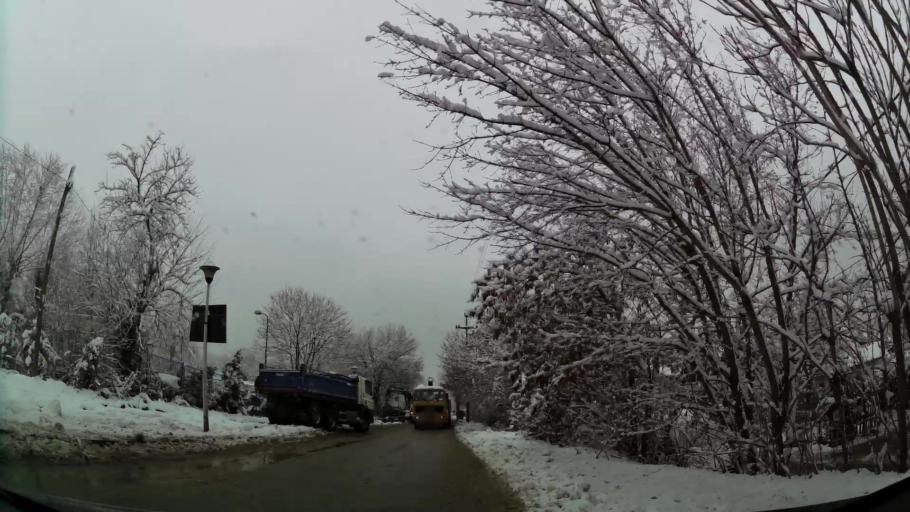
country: RS
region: Central Serbia
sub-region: Belgrade
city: Stari Grad
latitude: 44.8099
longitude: 20.4439
